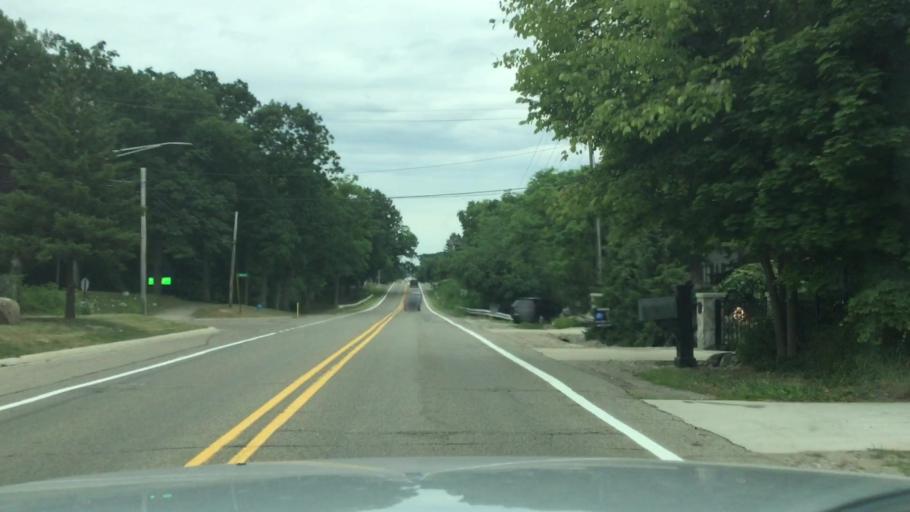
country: US
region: Michigan
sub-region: Oakland County
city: Sylvan Lake
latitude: 42.6707
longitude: -83.3472
